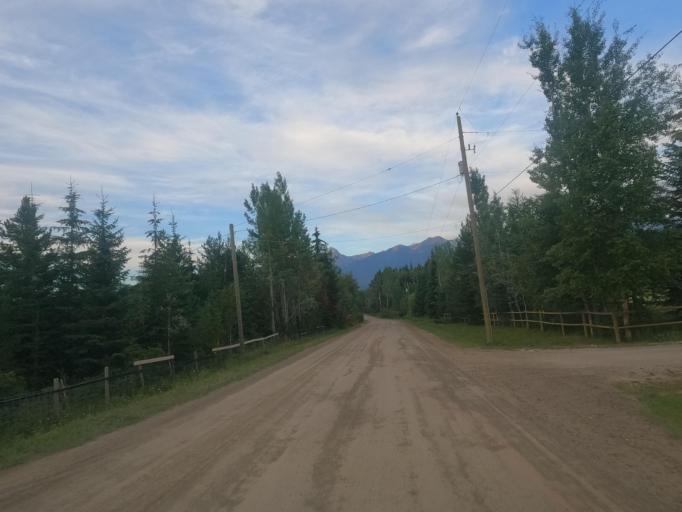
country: CA
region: British Columbia
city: Golden
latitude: 51.4438
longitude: -117.0383
